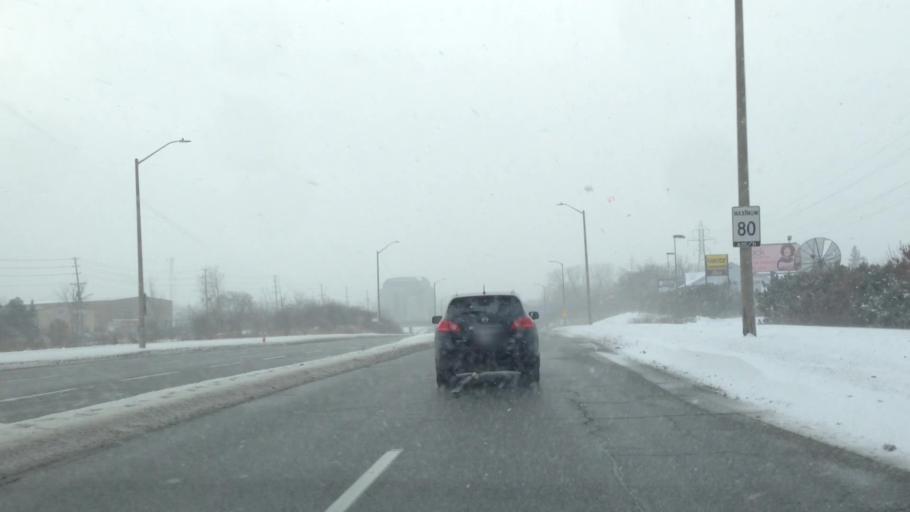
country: CA
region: Ontario
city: Ottawa
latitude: 45.4100
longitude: -75.6203
